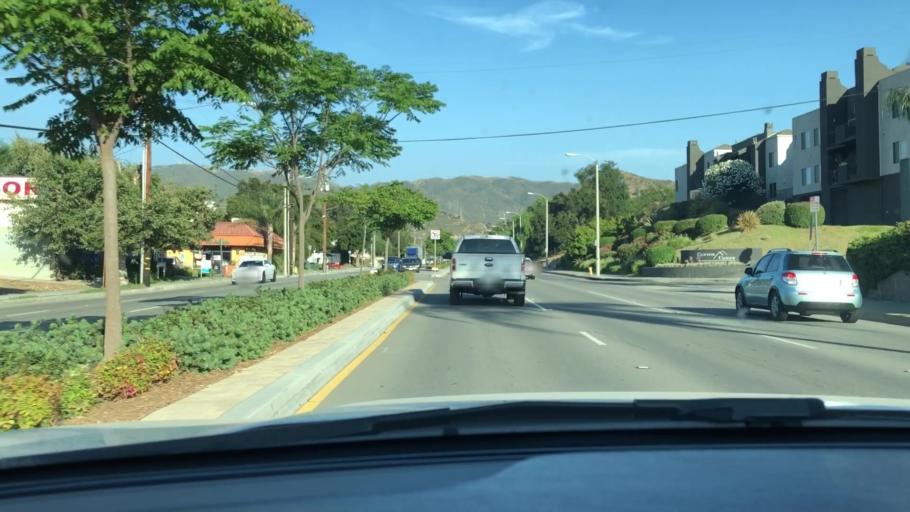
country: US
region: California
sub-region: Los Angeles County
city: Santa Clarita
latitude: 34.3701
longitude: -118.5136
